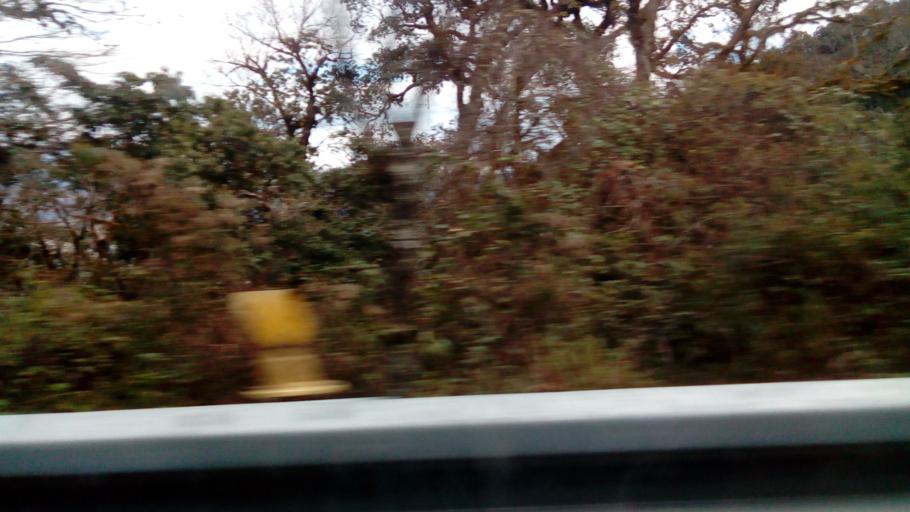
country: TW
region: Taiwan
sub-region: Hualien
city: Hualian
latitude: 24.3992
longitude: 121.3661
